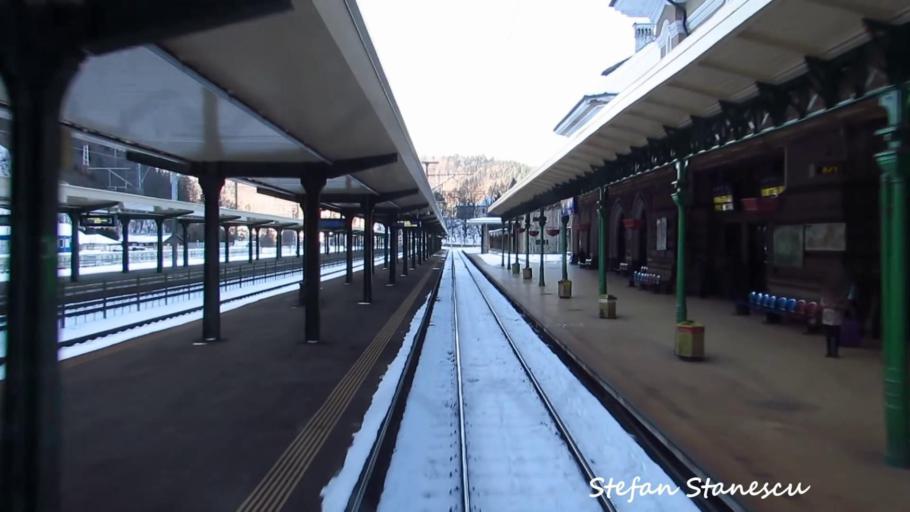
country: RO
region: Prahova
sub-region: Oras Sinaia
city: Sinaia
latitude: 45.3582
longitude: 25.5557
